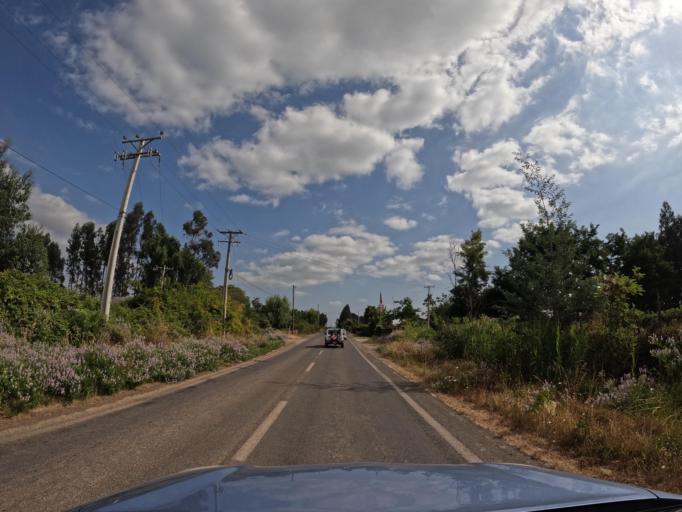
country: CL
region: Maule
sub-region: Provincia de Curico
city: Molina
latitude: -35.1982
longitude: -71.2974
